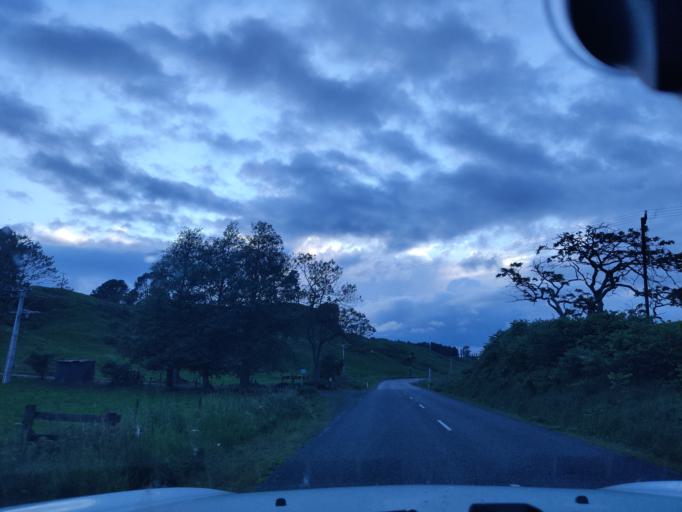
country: NZ
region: Waikato
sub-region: South Waikato District
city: Tokoroa
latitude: -38.1959
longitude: 175.8036
